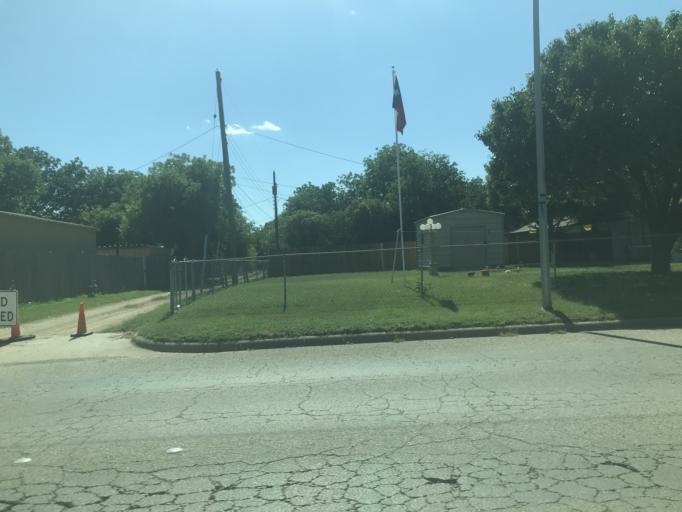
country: US
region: Texas
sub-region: Taylor County
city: Abilene
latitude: 32.4105
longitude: -99.7481
